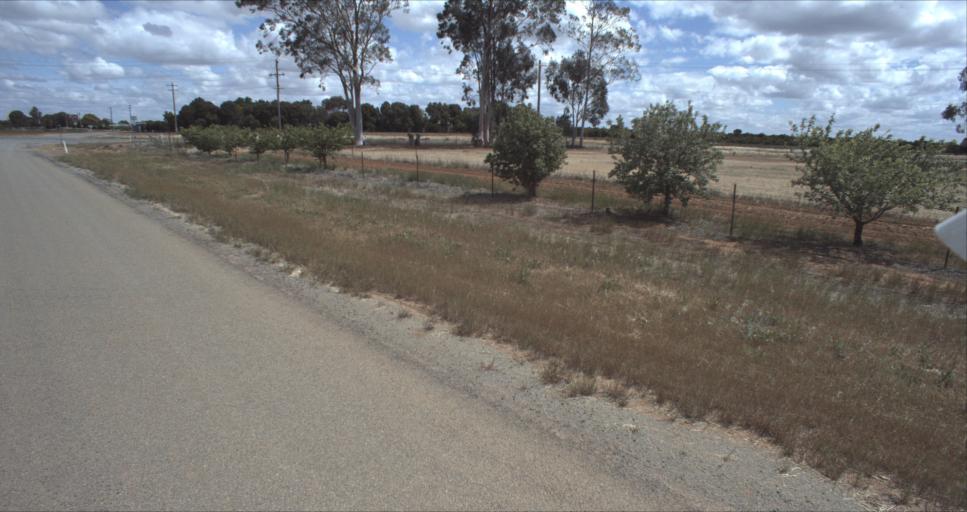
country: AU
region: New South Wales
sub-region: Leeton
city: Leeton
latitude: -34.5775
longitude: 146.3979
